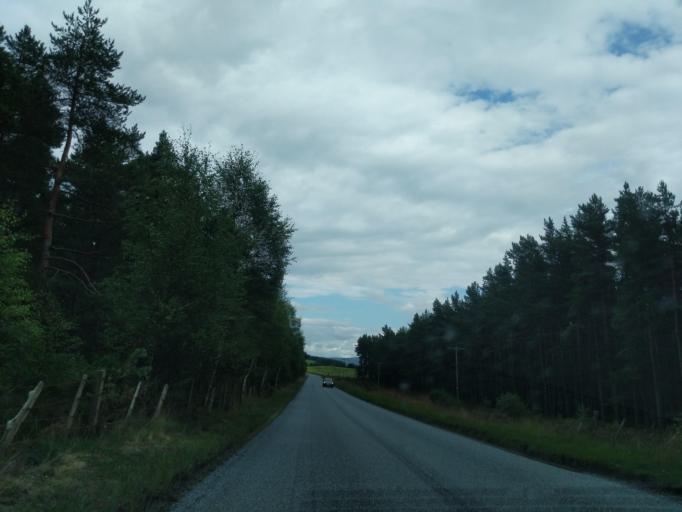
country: GB
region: Scotland
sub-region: Highland
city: Grantown on Spey
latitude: 57.3067
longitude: -3.7221
